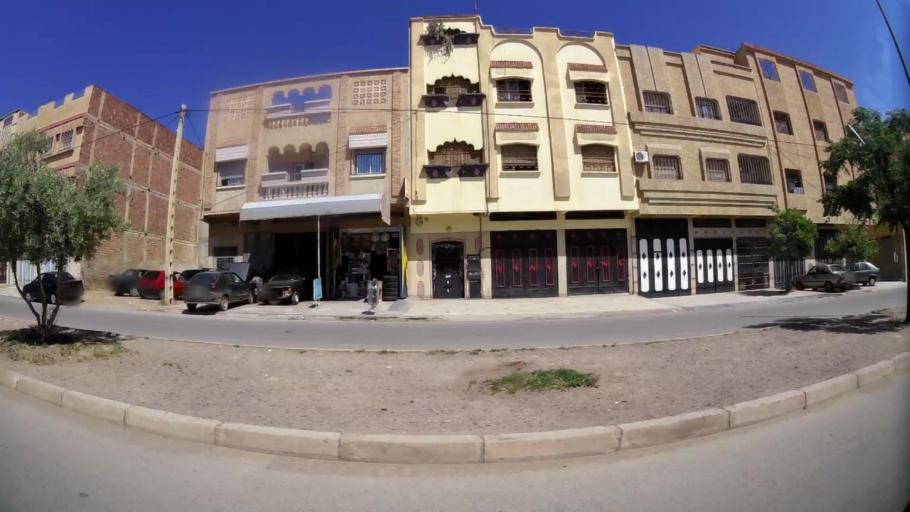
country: MA
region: Oriental
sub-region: Oujda-Angad
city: Oujda
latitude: 34.6716
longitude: -1.9422
